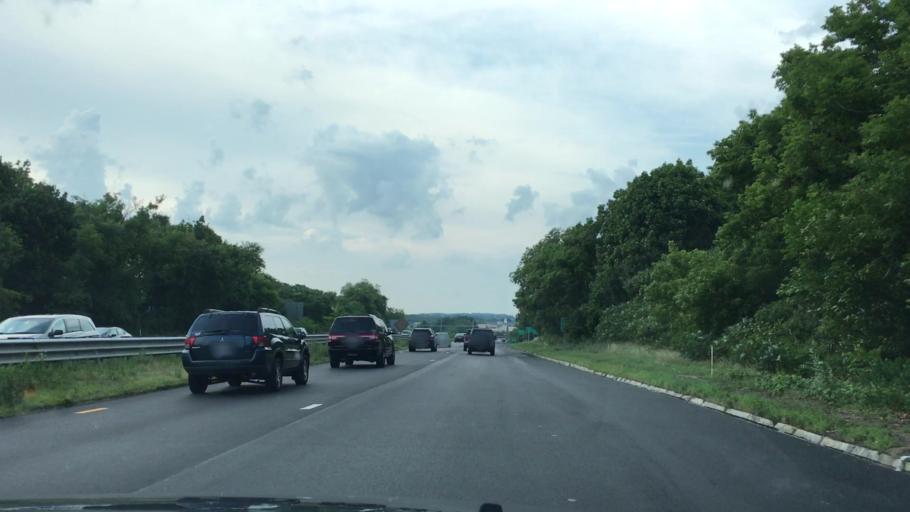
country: US
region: Massachusetts
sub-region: Essex County
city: Peabody
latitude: 42.5432
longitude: -70.9358
